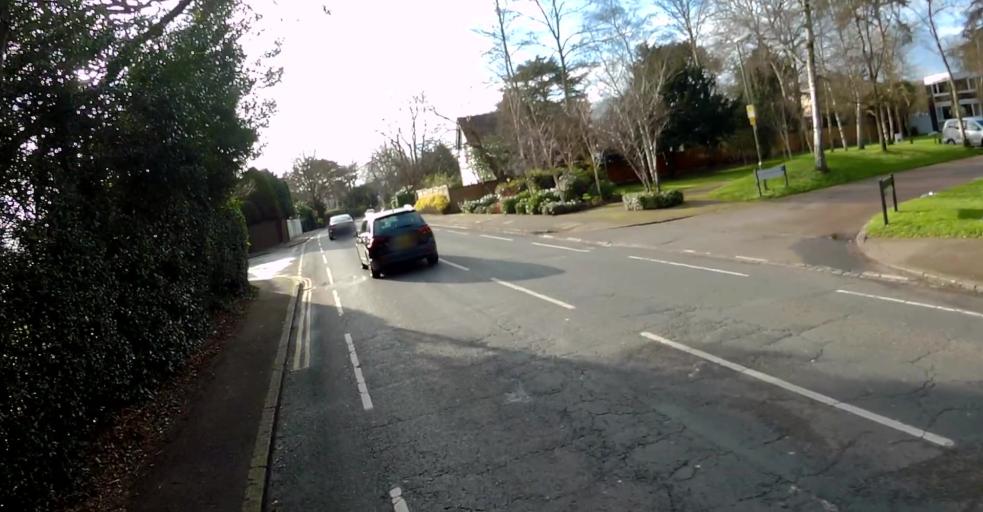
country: GB
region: England
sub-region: Surrey
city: Weybridge
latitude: 51.3754
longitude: -0.4370
